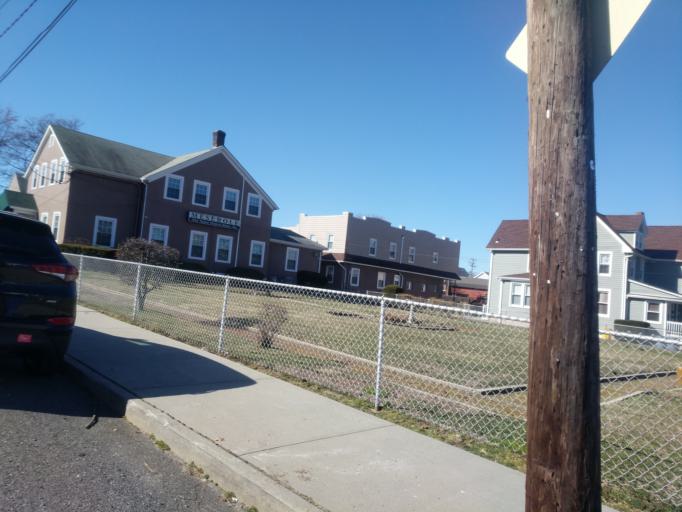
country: US
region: New York
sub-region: Nassau County
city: Inwood
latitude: 40.6165
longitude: -73.7454
